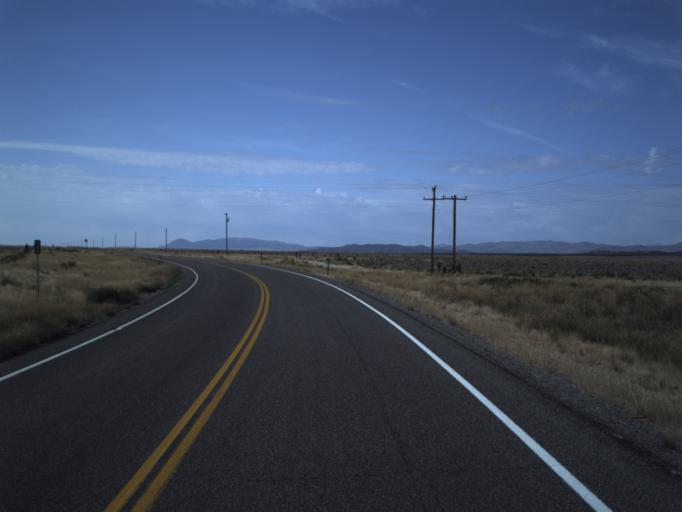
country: US
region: Idaho
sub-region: Cassia County
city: Burley
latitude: 41.7641
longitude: -113.5109
